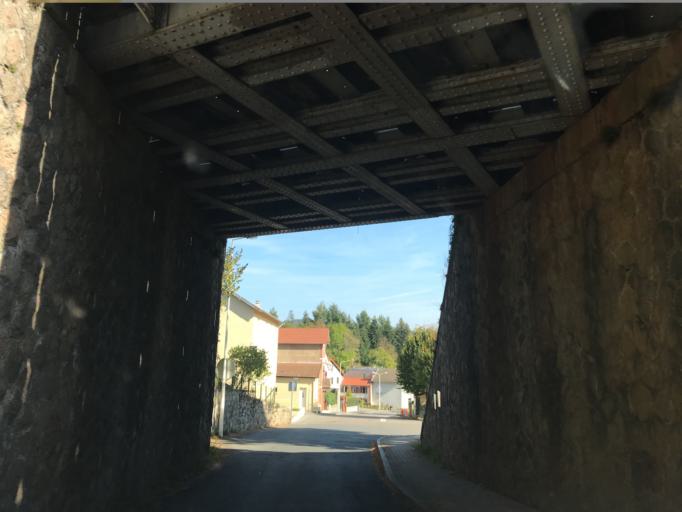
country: FR
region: Rhone-Alpes
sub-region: Departement de la Loire
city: Noiretable
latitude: 45.8173
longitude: 3.7617
